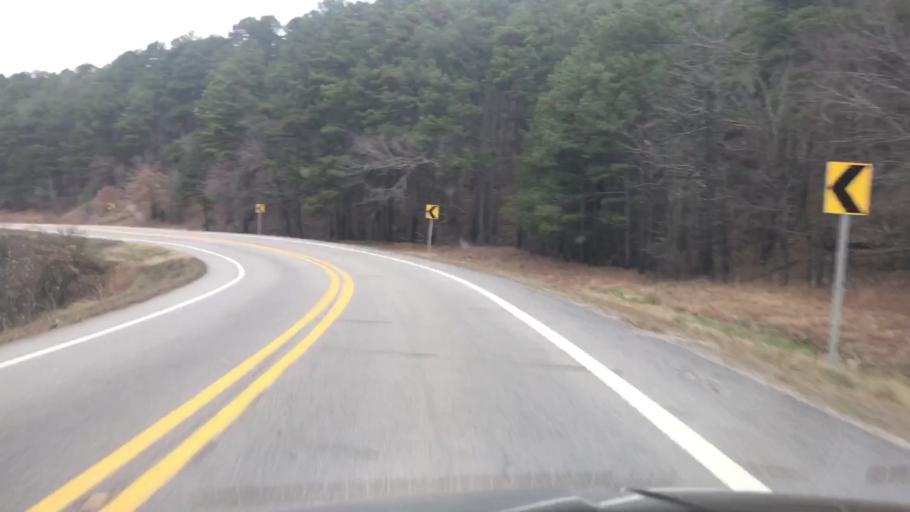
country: US
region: Arkansas
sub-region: Montgomery County
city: Mount Ida
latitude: 34.6832
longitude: -93.7982
